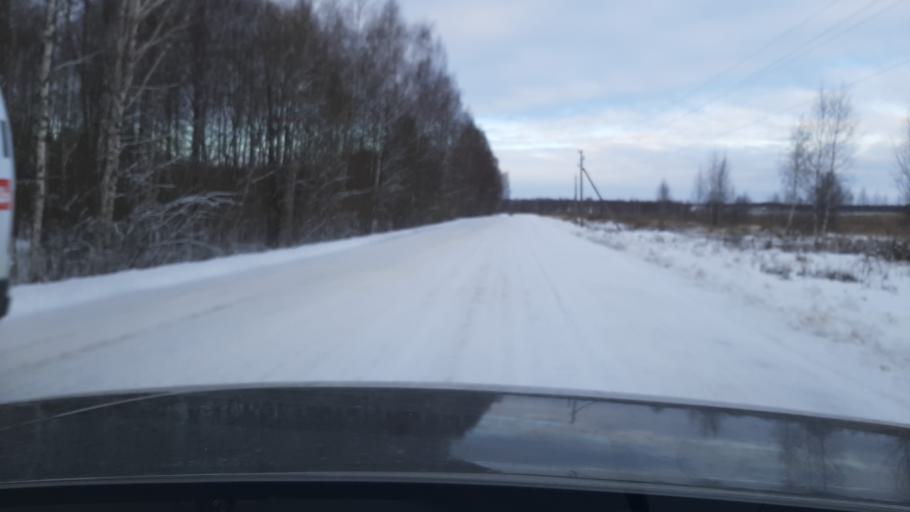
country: RU
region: Kostroma
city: Nerekhta
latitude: 57.4710
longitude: 40.6748
